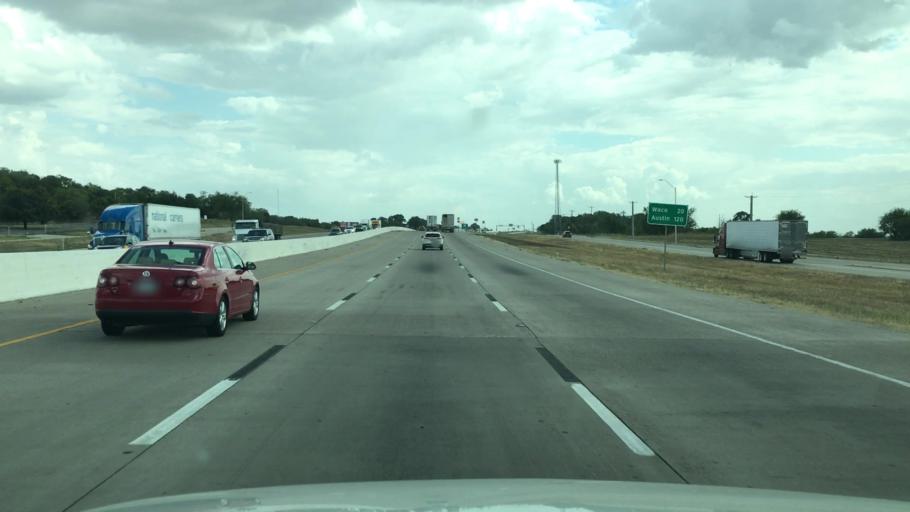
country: US
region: Texas
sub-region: McLennan County
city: West
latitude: 31.8152
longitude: -97.0985
